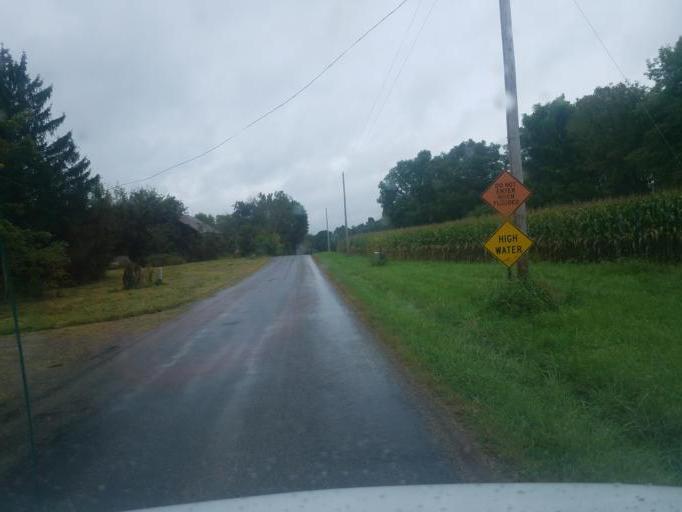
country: US
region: Ohio
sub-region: Wayne County
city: West Salem
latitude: 40.9564
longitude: -82.1190
